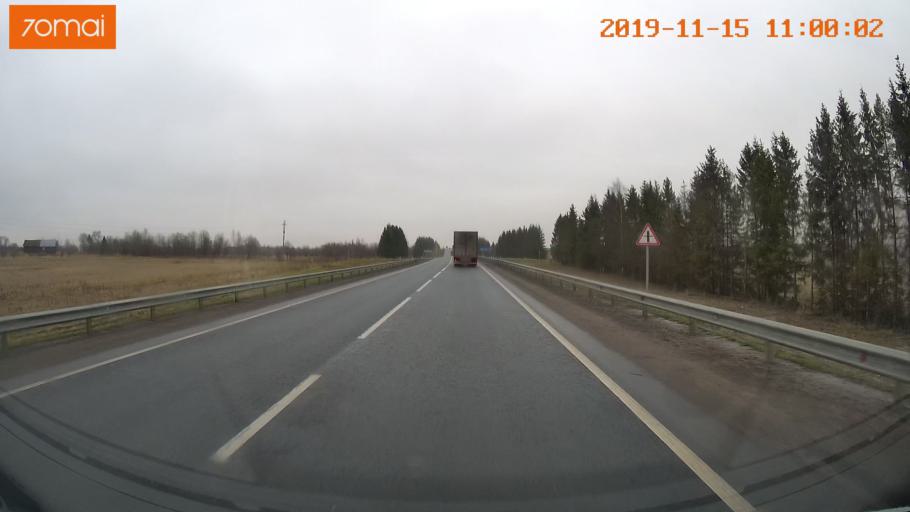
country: RU
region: Vologda
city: Chebsara
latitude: 59.1391
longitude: 38.8896
